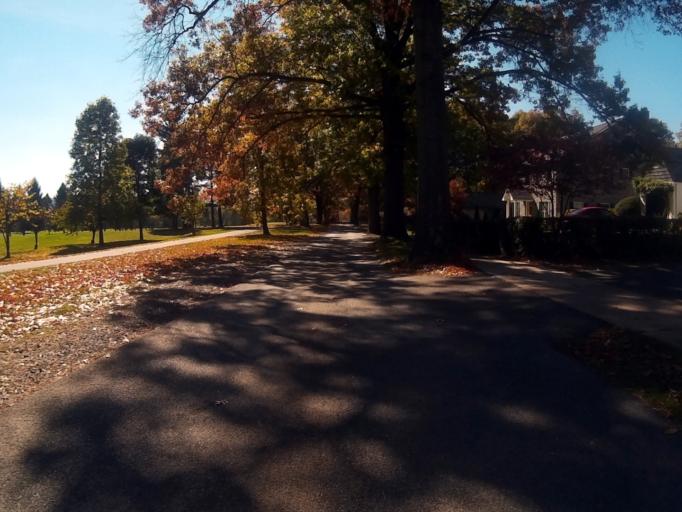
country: US
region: Pennsylvania
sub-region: Centre County
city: State College
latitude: 40.7947
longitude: -77.8743
